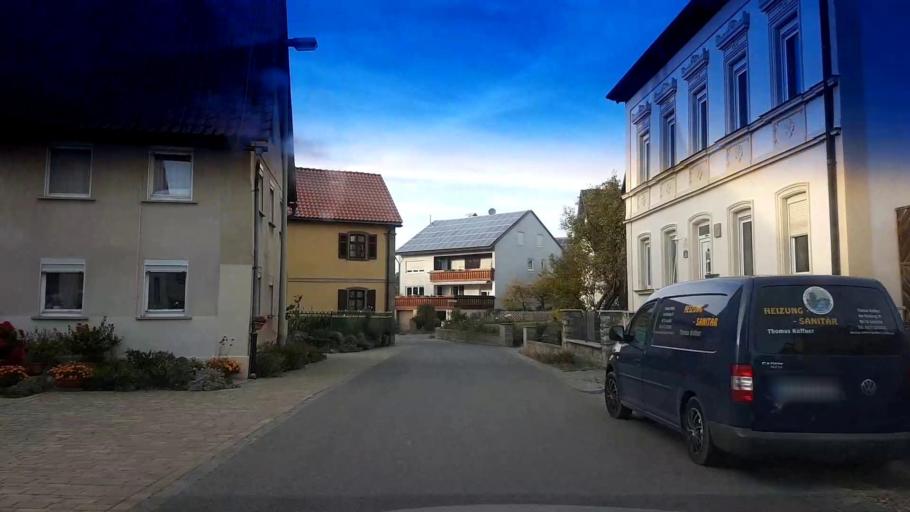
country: DE
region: Bavaria
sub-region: Upper Franconia
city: Schesslitz
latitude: 49.9708
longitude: 11.0595
